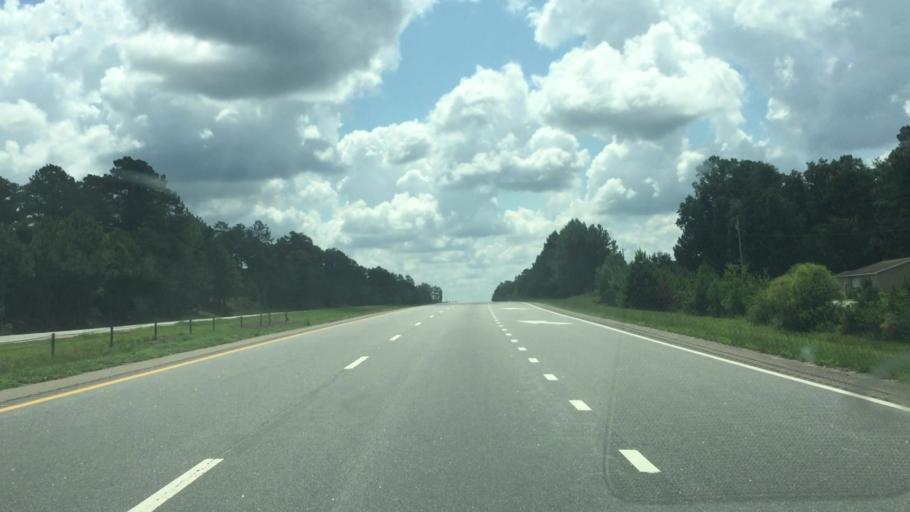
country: US
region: North Carolina
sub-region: Richmond County
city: Hamlet
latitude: 34.8669
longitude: -79.6414
